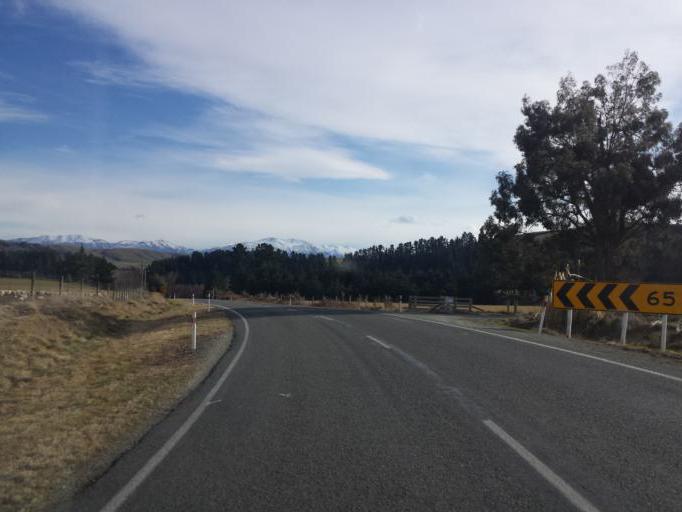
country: NZ
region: Canterbury
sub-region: Timaru District
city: Pleasant Point
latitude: -44.0856
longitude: 170.9851
